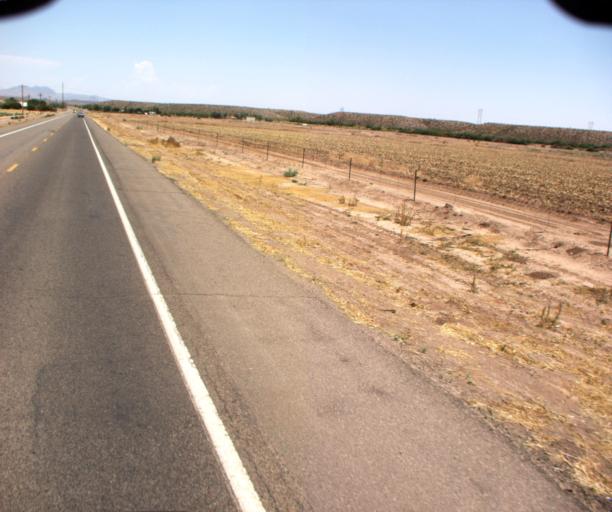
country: US
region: Arizona
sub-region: Graham County
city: Safford
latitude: 32.8128
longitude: -109.6130
